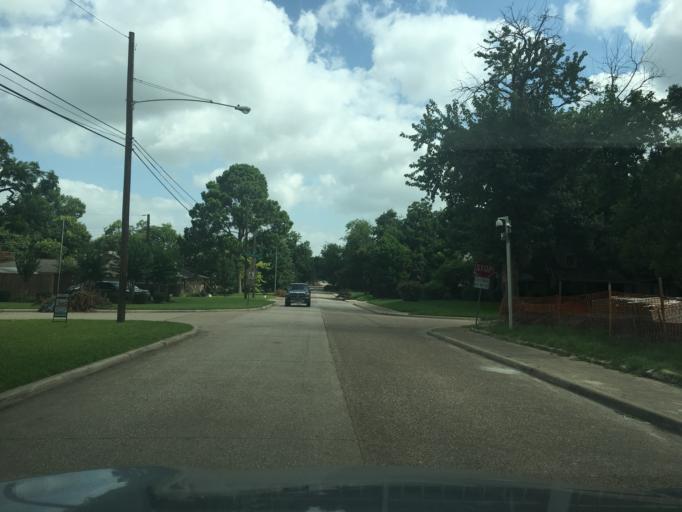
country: US
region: Texas
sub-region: Dallas County
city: Addison
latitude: 32.9129
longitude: -96.8340
